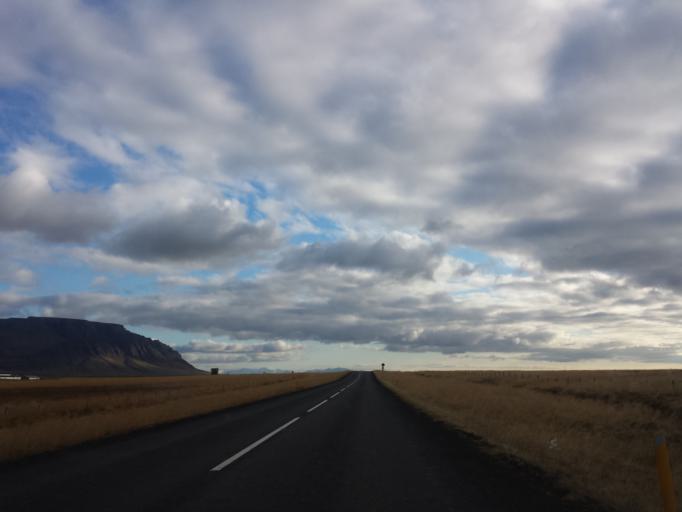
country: IS
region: West
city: Borgarnes
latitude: 64.8186
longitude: -22.2673
